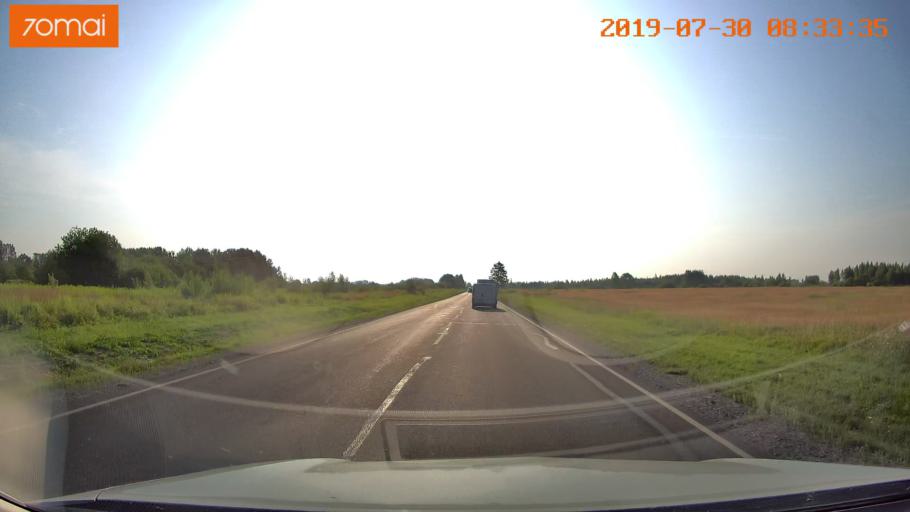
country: RU
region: Kaliningrad
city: Chernyakhovsk
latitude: 54.6359
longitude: 21.7484
